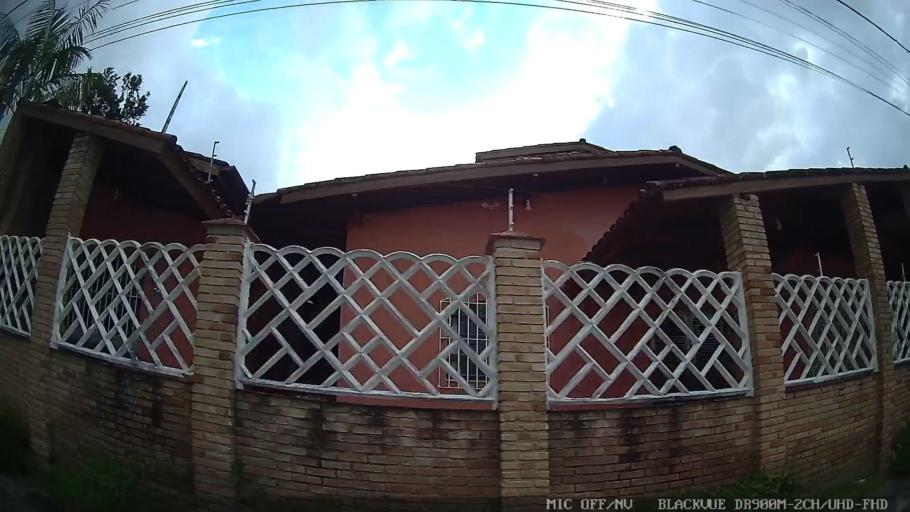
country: BR
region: Sao Paulo
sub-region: Caraguatatuba
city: Caraguatatuba
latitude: -23.6365
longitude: -45.4282
